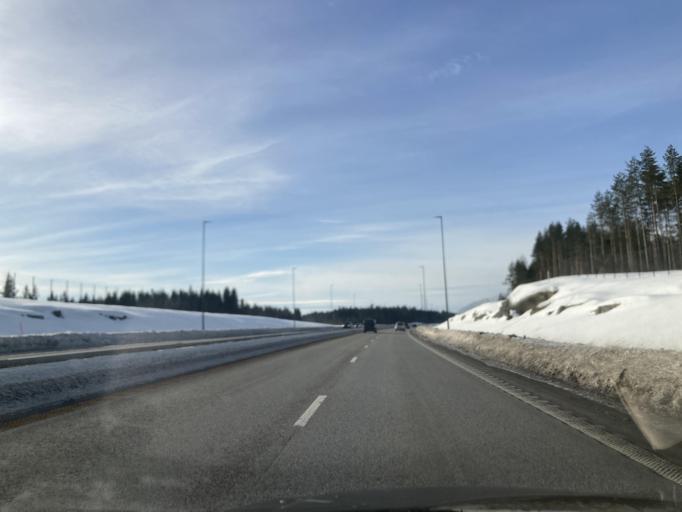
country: NO
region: Hedmark
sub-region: Loten
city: Loten
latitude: 60.8680
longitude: 11.4366
